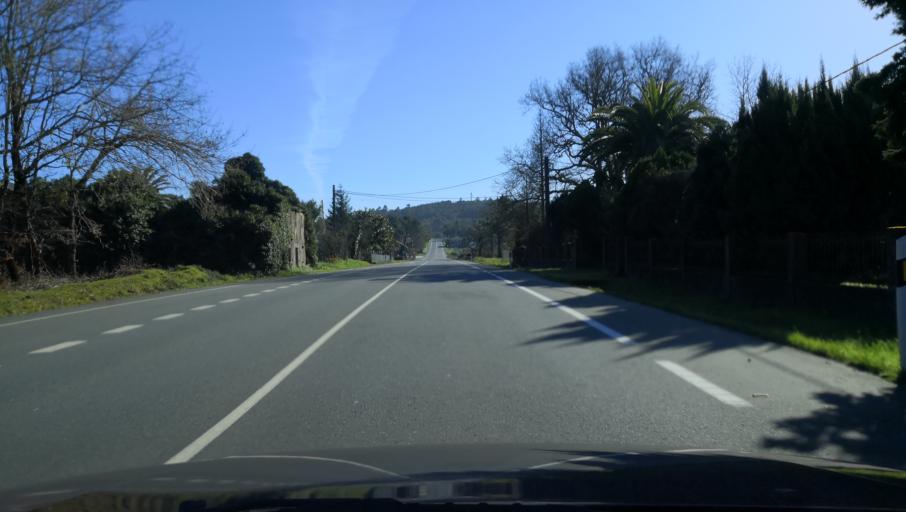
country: ES
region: Galicia
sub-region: Provincia da Coruna
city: Ribeira
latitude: 42.7566
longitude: -8.3635
